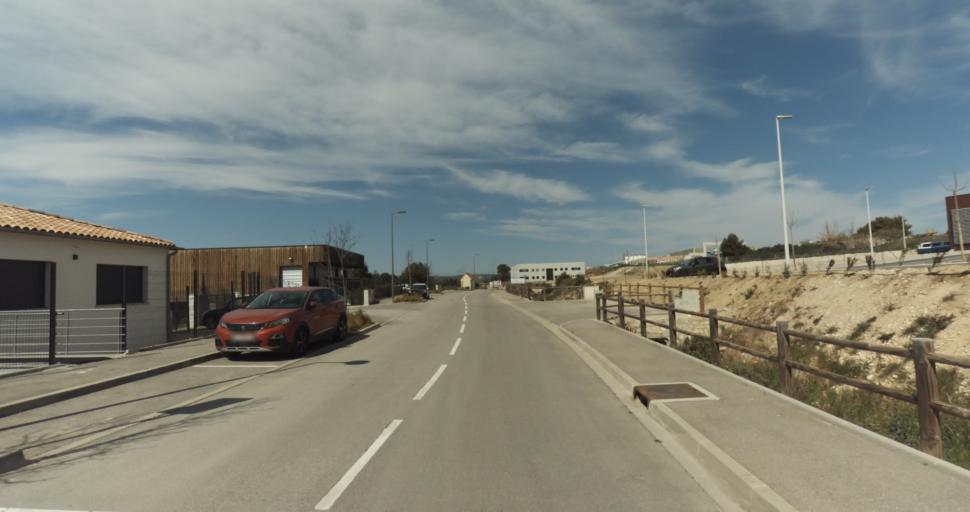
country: FR
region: Provence-Alpes-Cote d'Azur
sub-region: Departement des Bouches-du-Rhone
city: Lambesc
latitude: 43.6446
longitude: 5.2537
